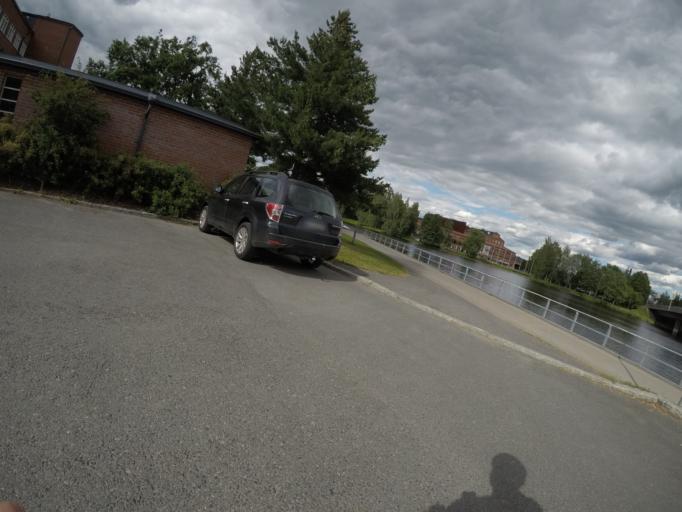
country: FI
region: Haeme
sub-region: Haemeenlinna
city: Haemeenlinna
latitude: 60.9957
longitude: 24.4732
